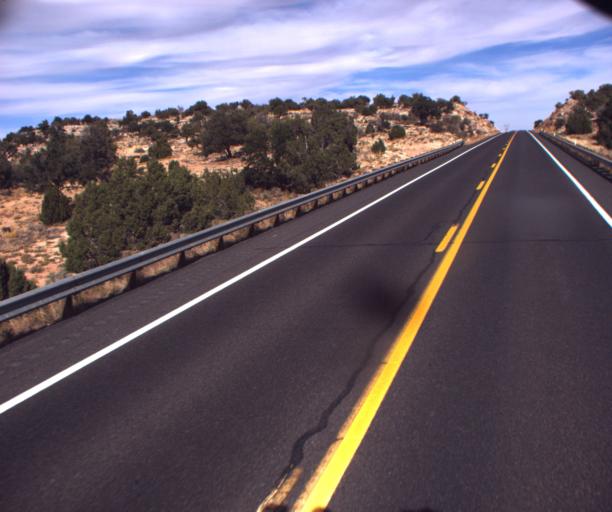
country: US
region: Arizona
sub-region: Navajo County
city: Kayenta
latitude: 36.6826
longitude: -110.3830
